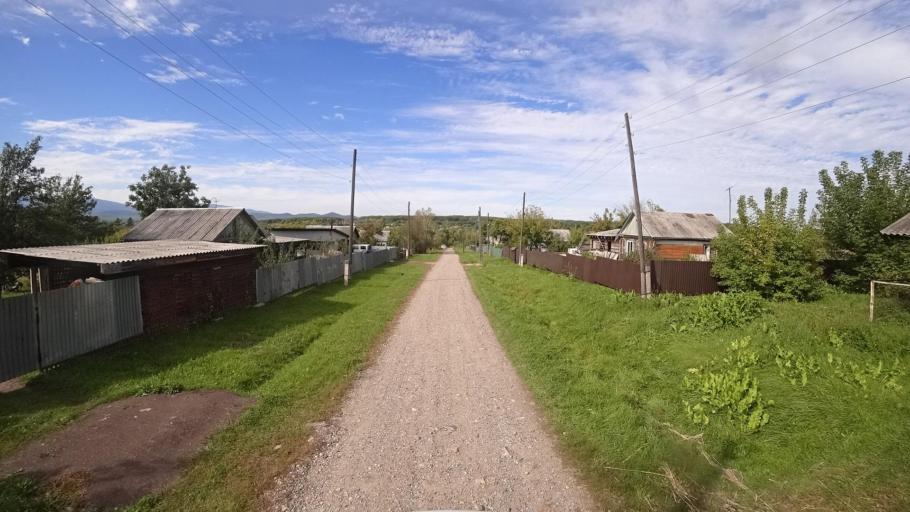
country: RU
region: Primorskiy
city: Dostoyevka
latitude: 44.3251
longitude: 133.4868
